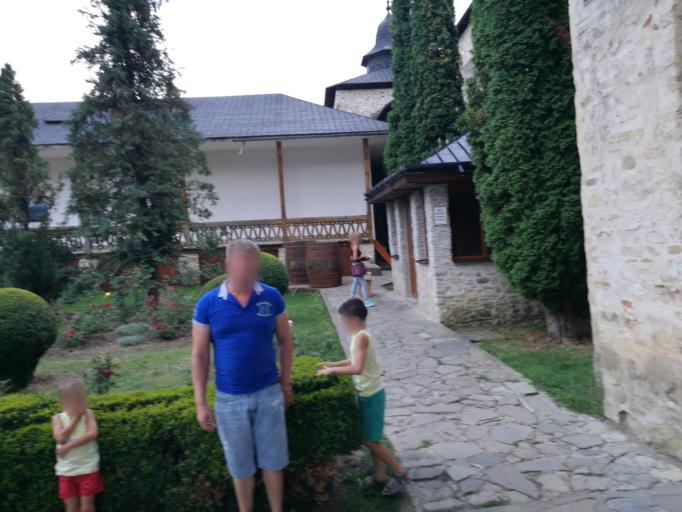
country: RO
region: Neamt
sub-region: Comuna Pipirig
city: Stanca
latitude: 47.2002
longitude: 26.1844
